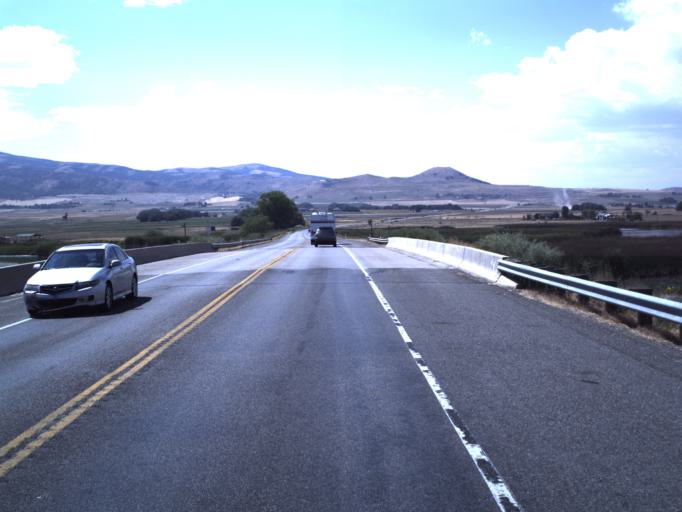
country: US
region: Utah
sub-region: Cache County
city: Mendon
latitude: 41.7462
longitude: -111.9521
